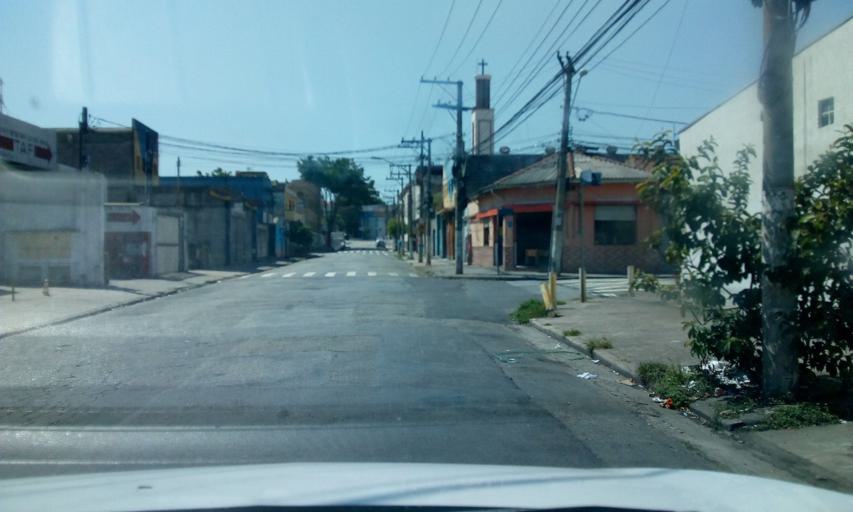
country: BR
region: Sao Paulo
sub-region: Osasco
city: Osasco
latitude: -23.5155
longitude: -46.7228
